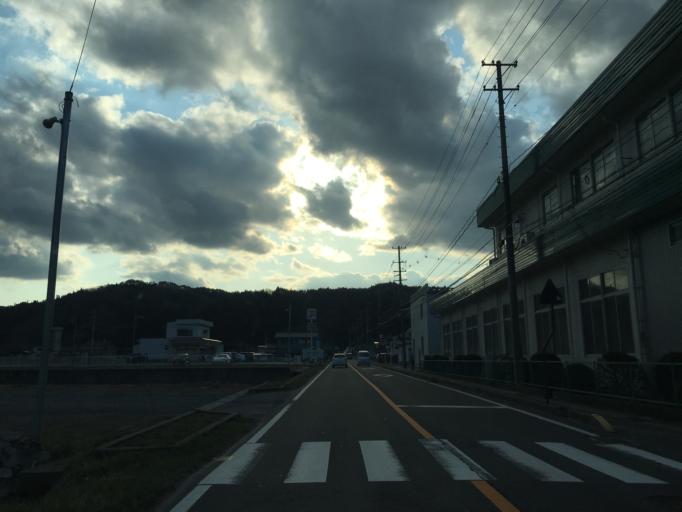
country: JP
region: Fukushima
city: Ishikawa
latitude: 37.0943
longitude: 140.5363
